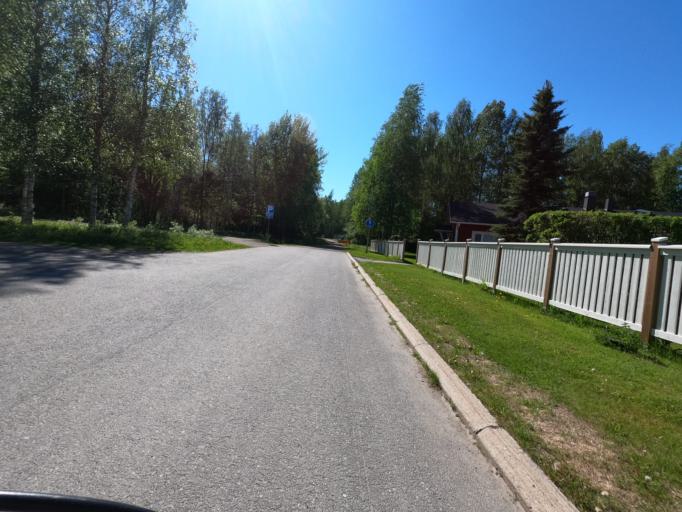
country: FI
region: North Karelia
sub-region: Joensuu
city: Joensuu
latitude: 62.6011
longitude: 29.8237
